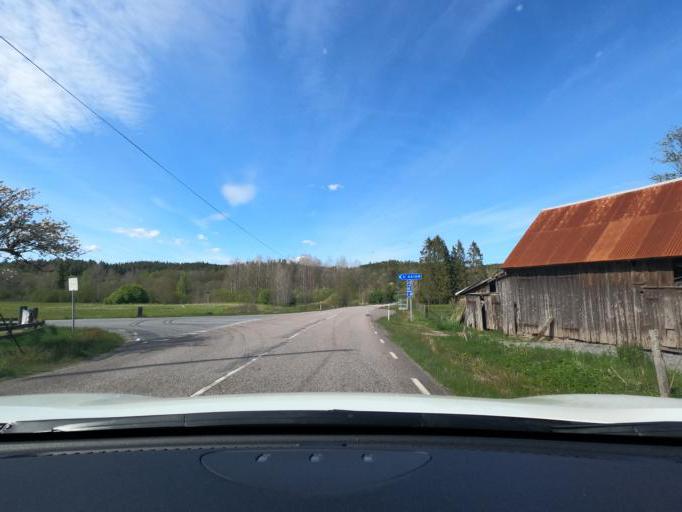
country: SE
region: Vaestra Goetaland
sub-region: Marks Kommun
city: Kinna
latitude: 57.4749
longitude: 12.5933
